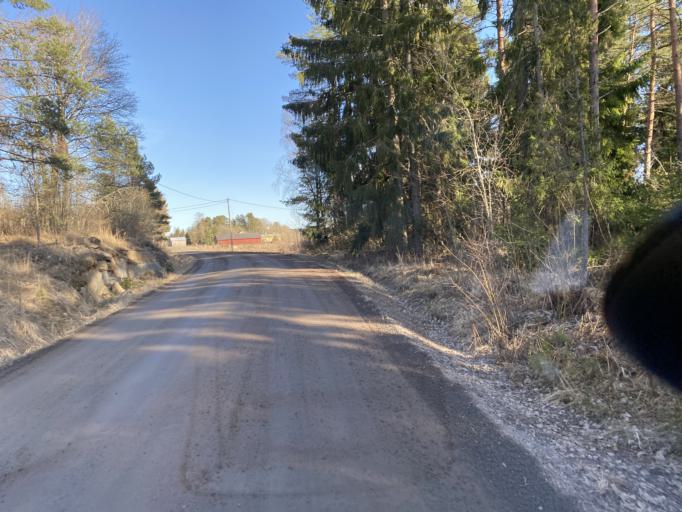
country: FI
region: Satakunta
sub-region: Rauma
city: Lappi
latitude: 61.1415
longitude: 21.9349
